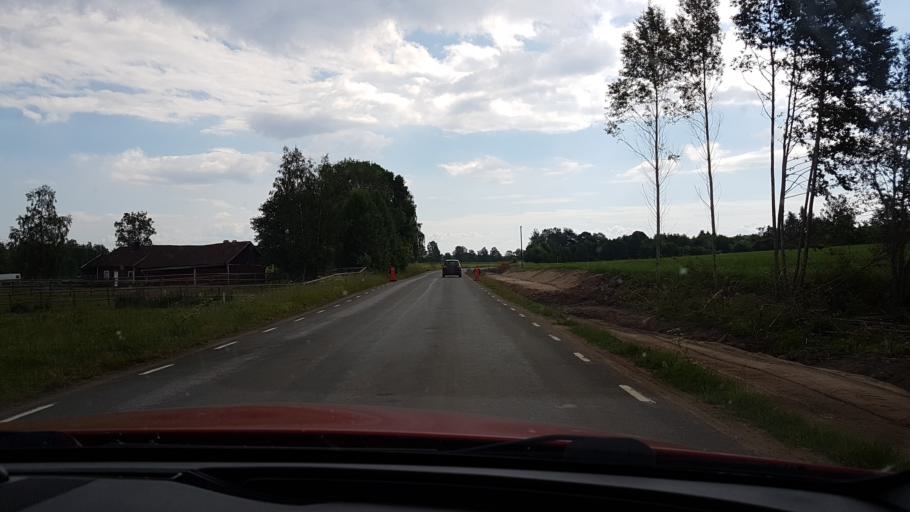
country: SE
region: Vaestra Goetaland
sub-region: Hjo Kommun
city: Hjo
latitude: 58.3067
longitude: 14.2389
